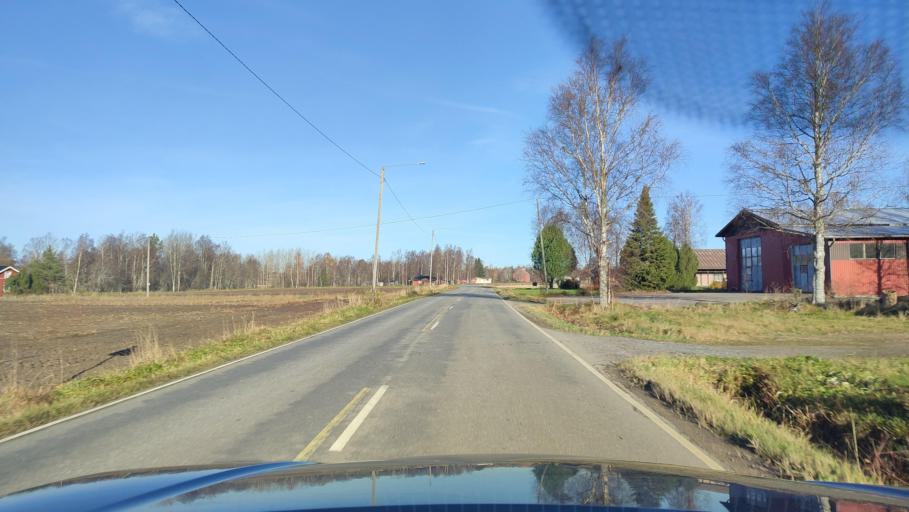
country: FI
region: Southern Ostrobothnia
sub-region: Suupohja
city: Karijoki
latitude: 62.2730
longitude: 21.7078
